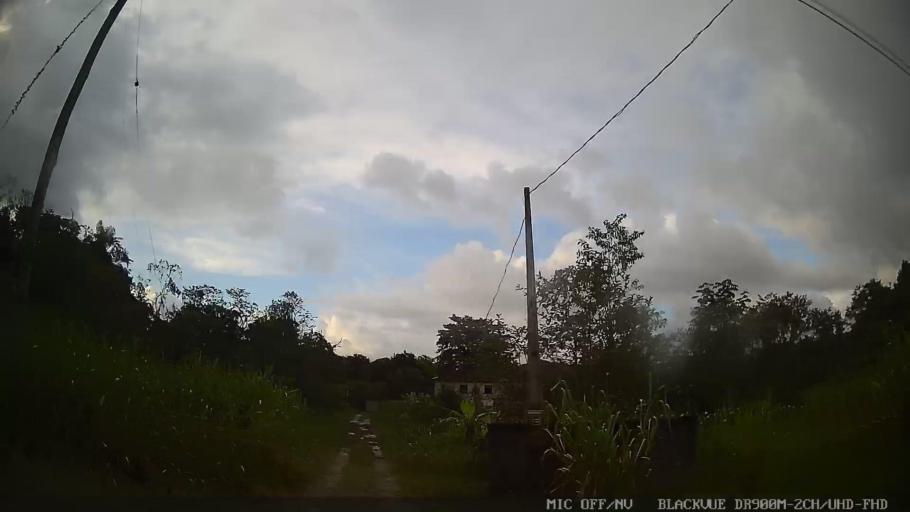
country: BR
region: Sao Paulo
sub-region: Itanhaem
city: Itanhaem
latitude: -24.1138
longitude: -46.7906
